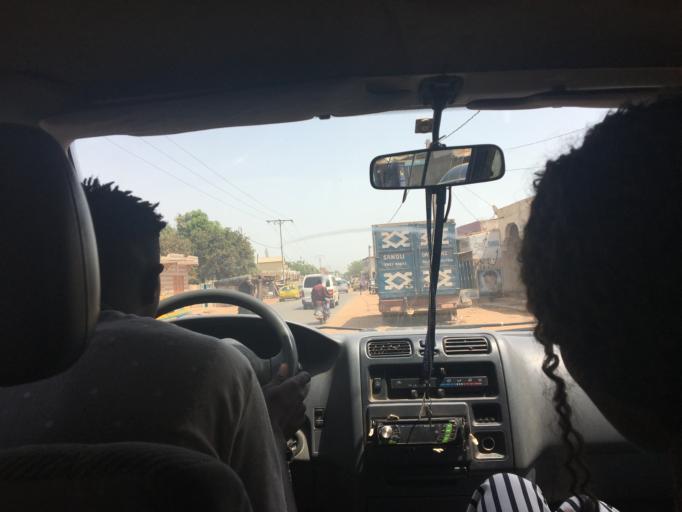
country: GM
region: Western
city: Abuko
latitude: 13.3906
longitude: -16.6751
